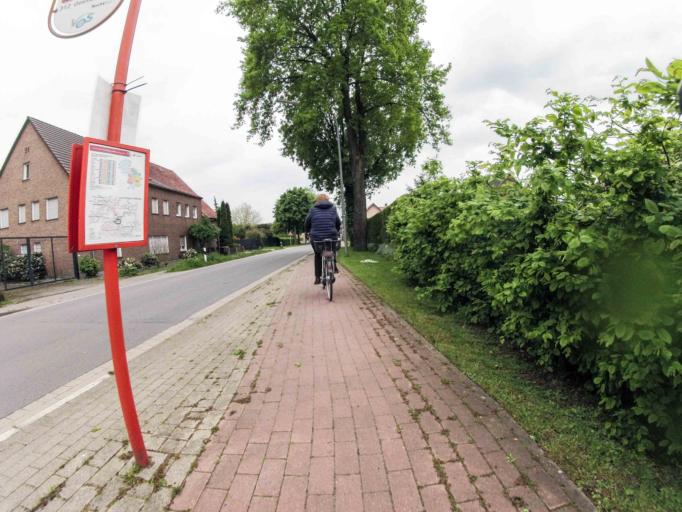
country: DE
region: Lower Saxony
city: Melle
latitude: 52.2371
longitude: 8.2805
